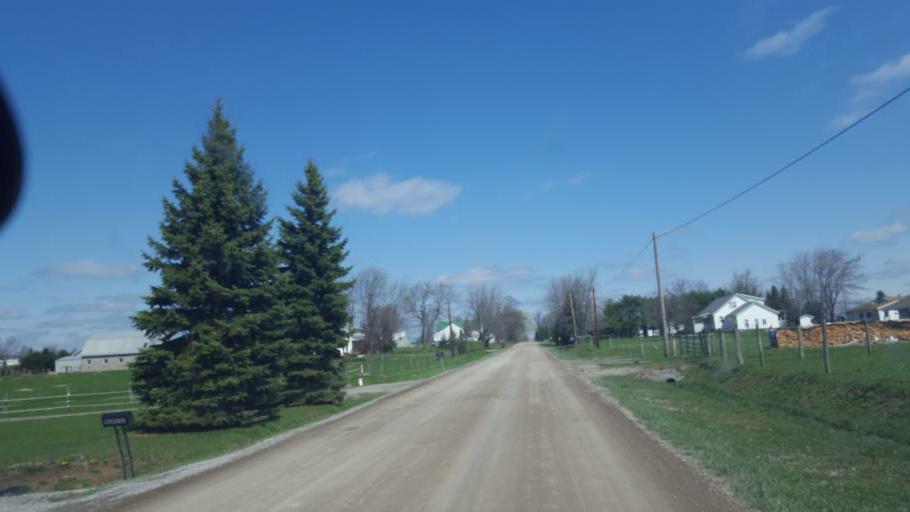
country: US
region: Ohio
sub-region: Geauga County
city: Middlefield
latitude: 41.4107
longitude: -81.0802
